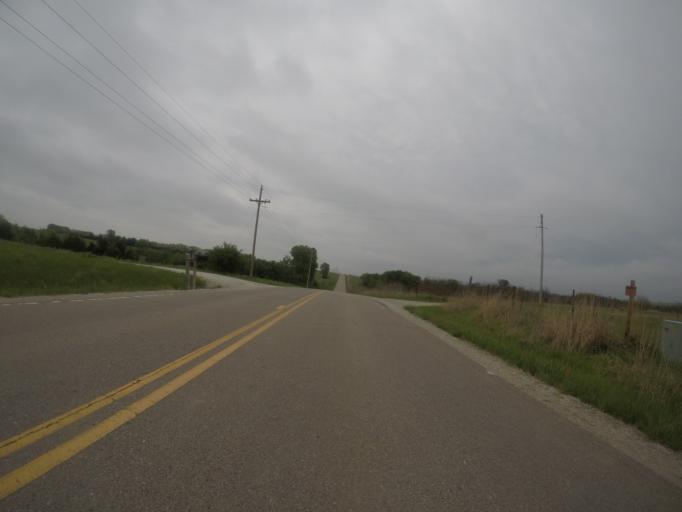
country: US
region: Kansas
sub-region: Pottawatomie County
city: Westmoreland
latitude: 39.5223
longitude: -96.2521
